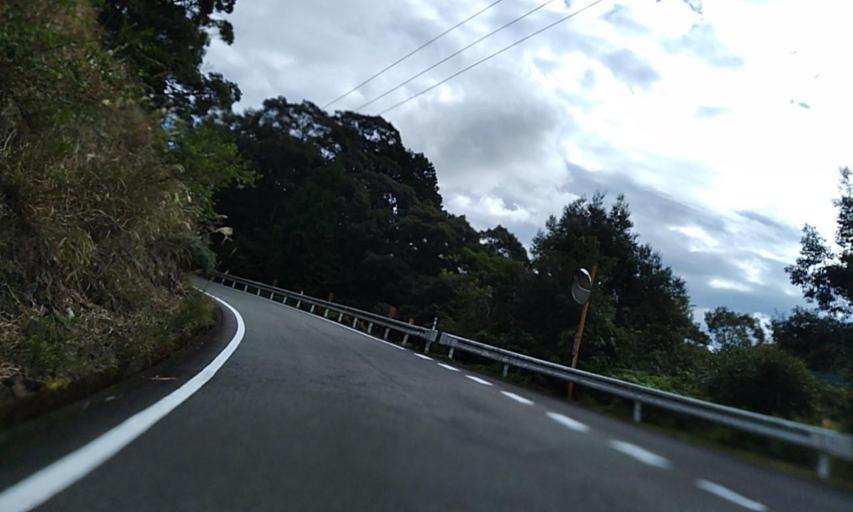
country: JP
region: Wakayama
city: Shingu
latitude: 33.5425
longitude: 135.8351
